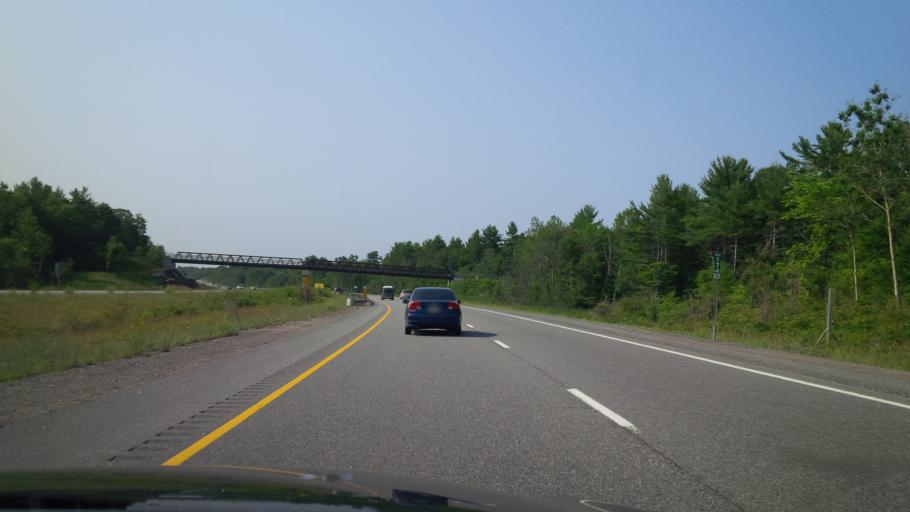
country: CA
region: Ontario
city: Gravenhurst
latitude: 44.9338
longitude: -79.3441
